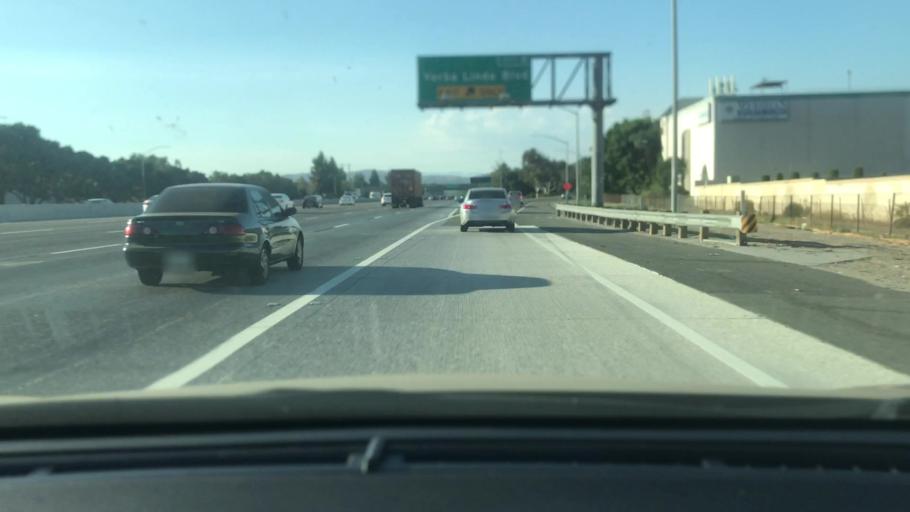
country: US
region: California
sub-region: Orange County
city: Placentia
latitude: 33.8752
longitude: -117.8789
